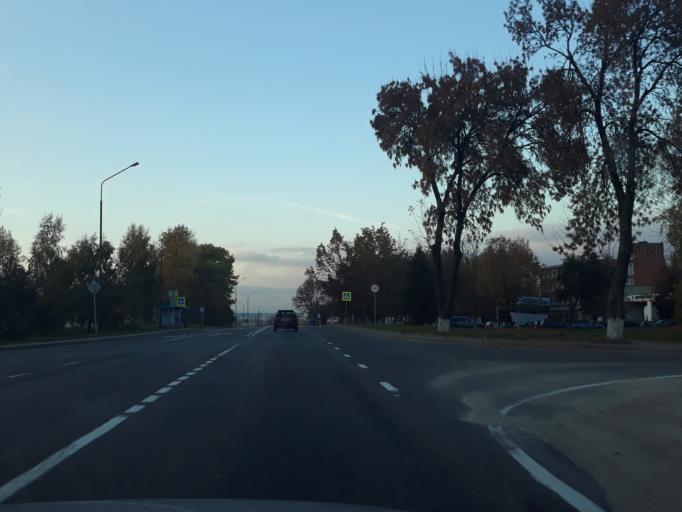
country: BY
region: Grodnenskaya
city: Vawkavysk
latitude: 53.1476
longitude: 24.4620
